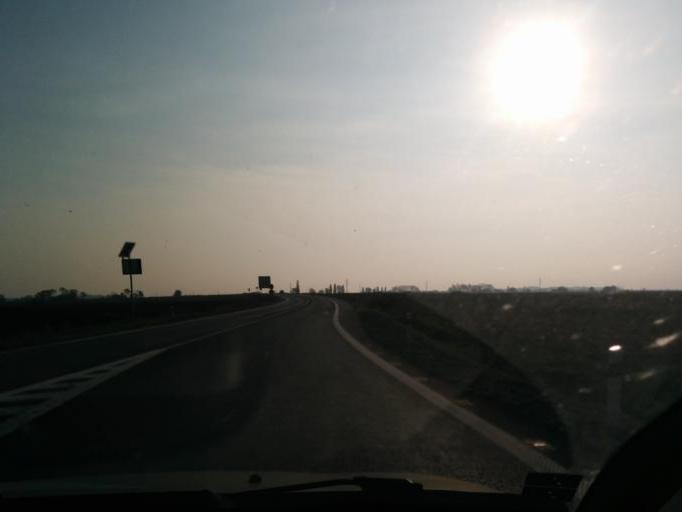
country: SK
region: Trnavsky
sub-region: Okres Galanta
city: Galanta
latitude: 48.2605
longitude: 17.7127
